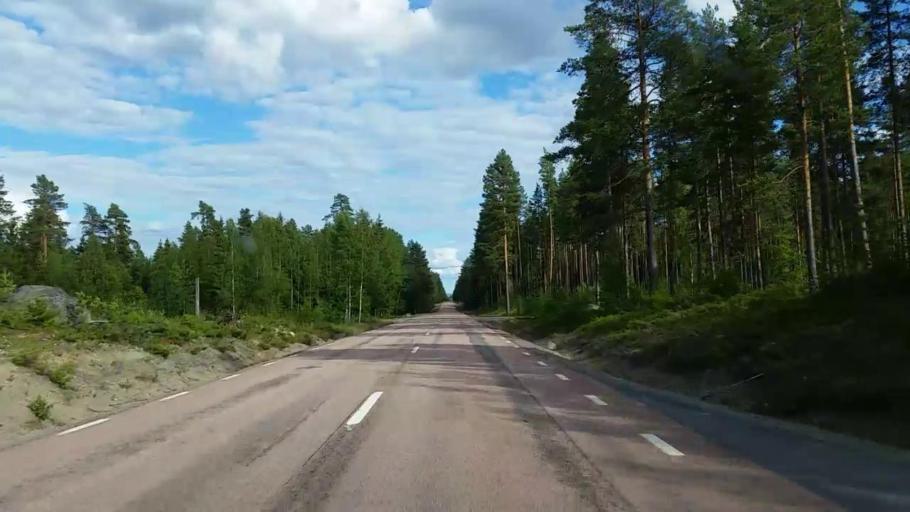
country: SE
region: Gaevleborg
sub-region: Ljusdals Kommun
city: Farila
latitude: 61.8876
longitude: 15.9275
